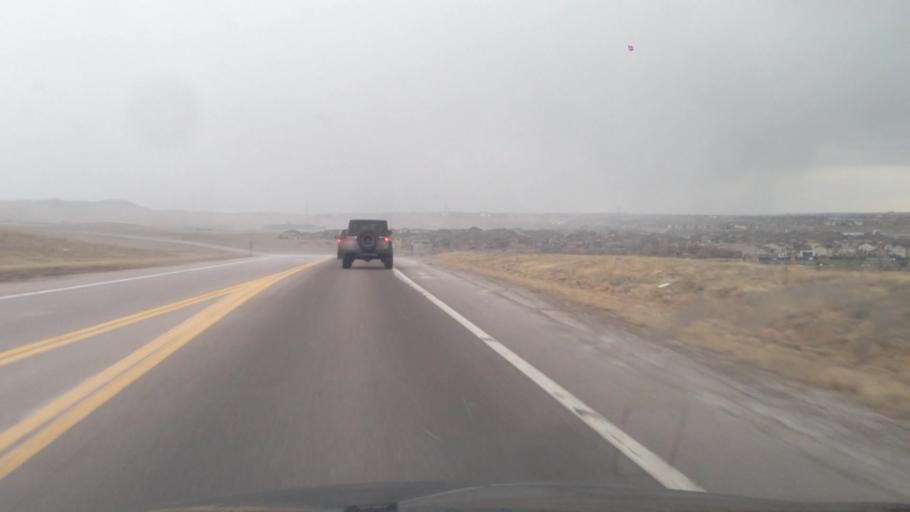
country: US
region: Colorado
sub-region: Douglas County
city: Stonegate
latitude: 39.4936
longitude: -104.8138
